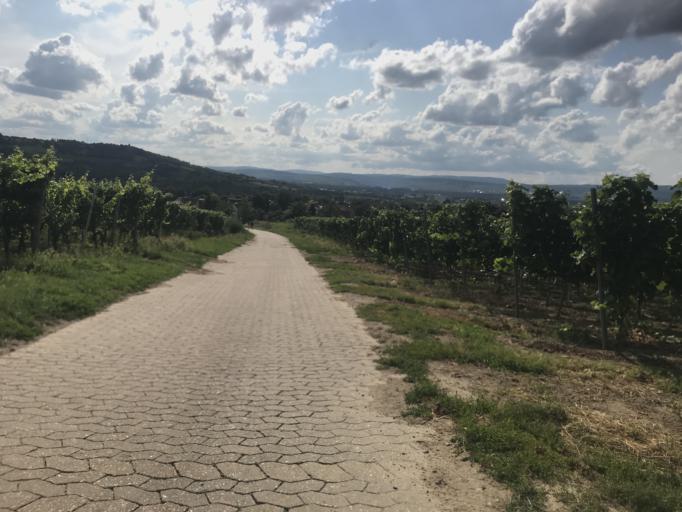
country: DE
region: Rheinland-Pfalz
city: Ingelheim am Rhein
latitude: 49.9681
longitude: 8.0678
